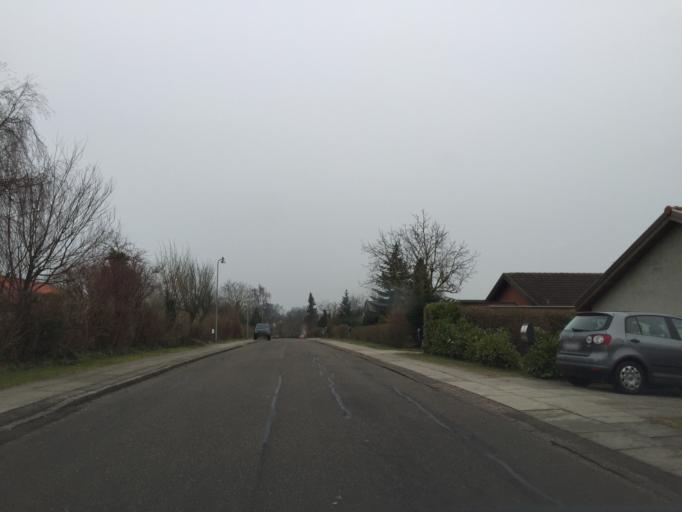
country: DK
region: Capital Region
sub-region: Fureso Kommune
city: Farum
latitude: 55.8117
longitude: 12.3623
